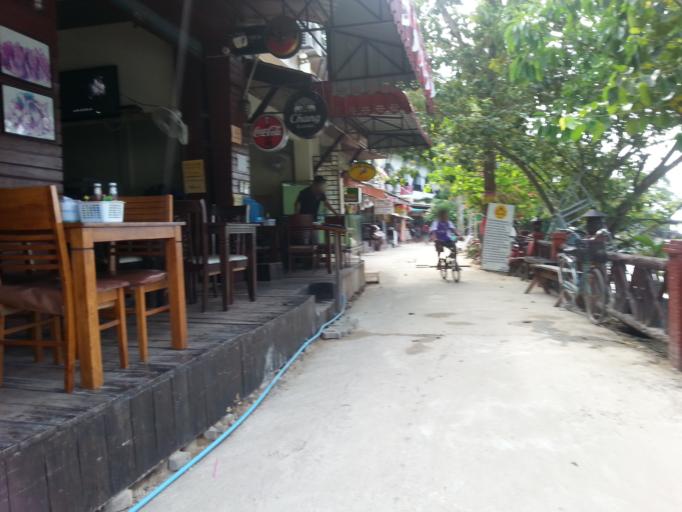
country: TH
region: Phangnga
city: Ban Phru Nai
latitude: 7.7374
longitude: 98.7741
